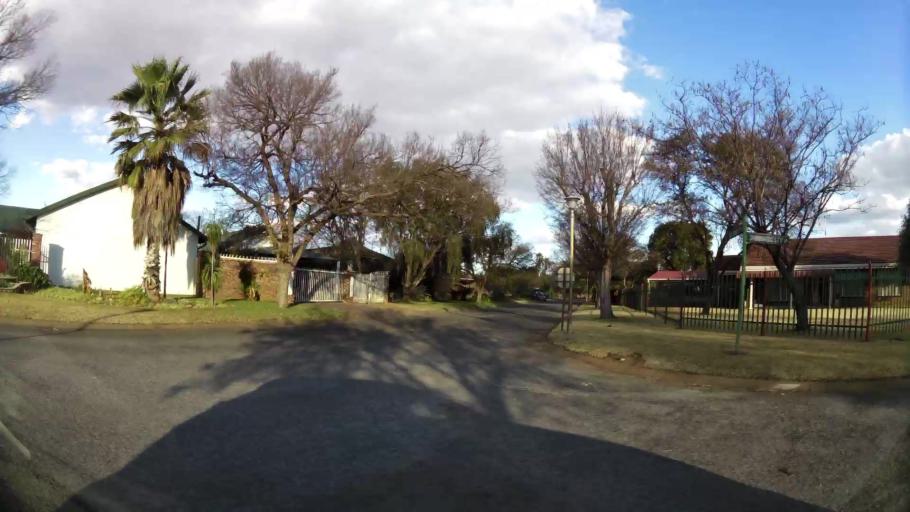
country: ZA
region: North-West
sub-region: Dr Kenneth Kaunda District Municipality
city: Potchefstroom
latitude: -26.7219
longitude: 27.0819
